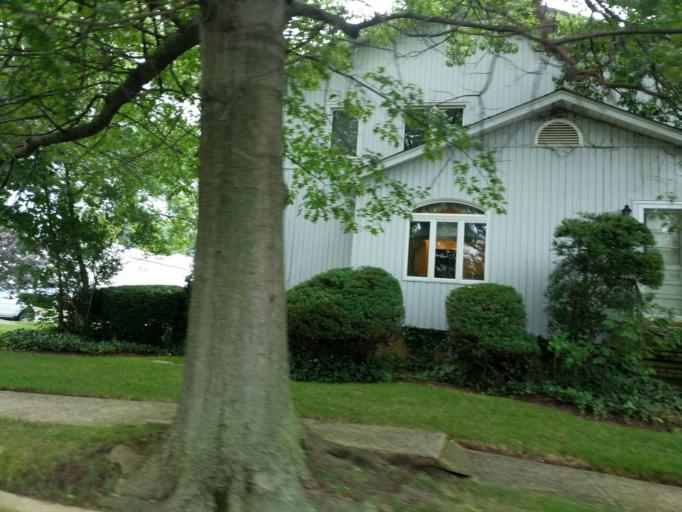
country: US
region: New York
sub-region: Nassau County
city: South Valley Stream
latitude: 40.6475
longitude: -73.7218
